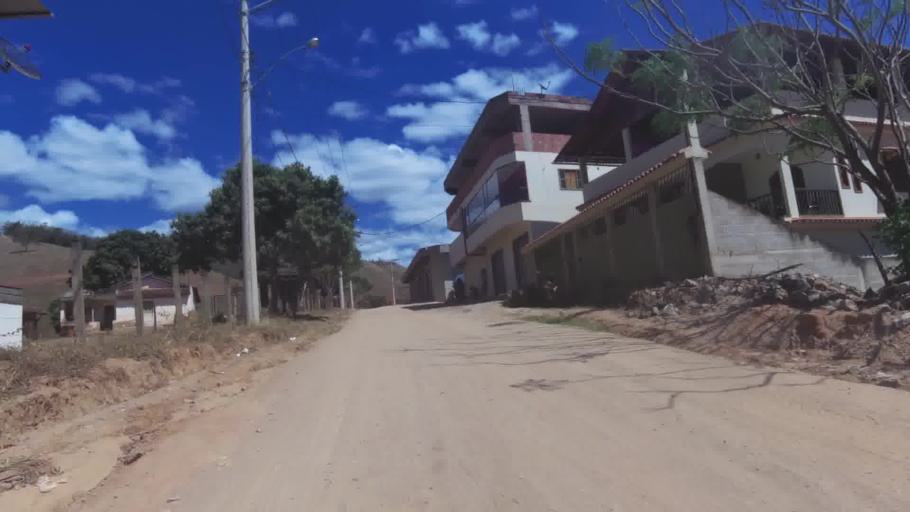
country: BR
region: Espirito Santo
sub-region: Cachoeiro De Itapemirim
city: Cachoeiro de Itapemirim
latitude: -20.9214
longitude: -41.1889
